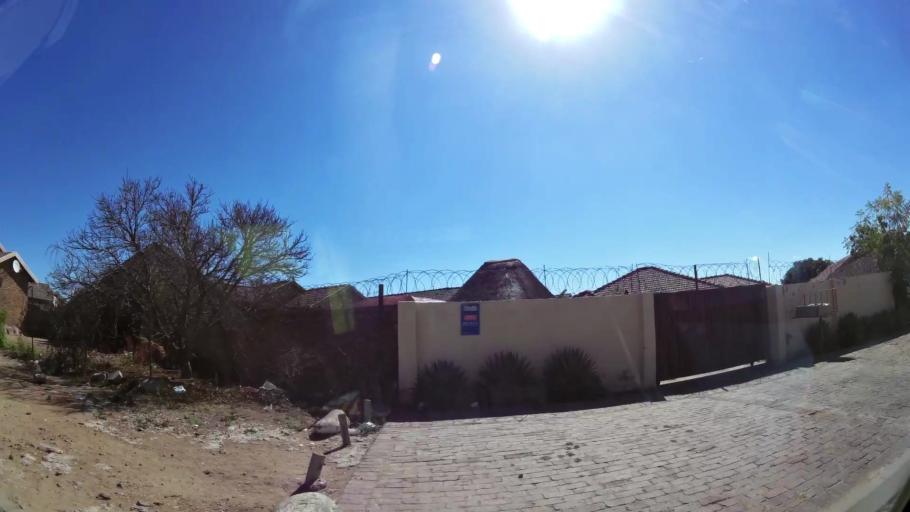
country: ZA
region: Limpopo
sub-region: Capricorn District Municipality
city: Polokwane
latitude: -23.8681
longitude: 29.4291
